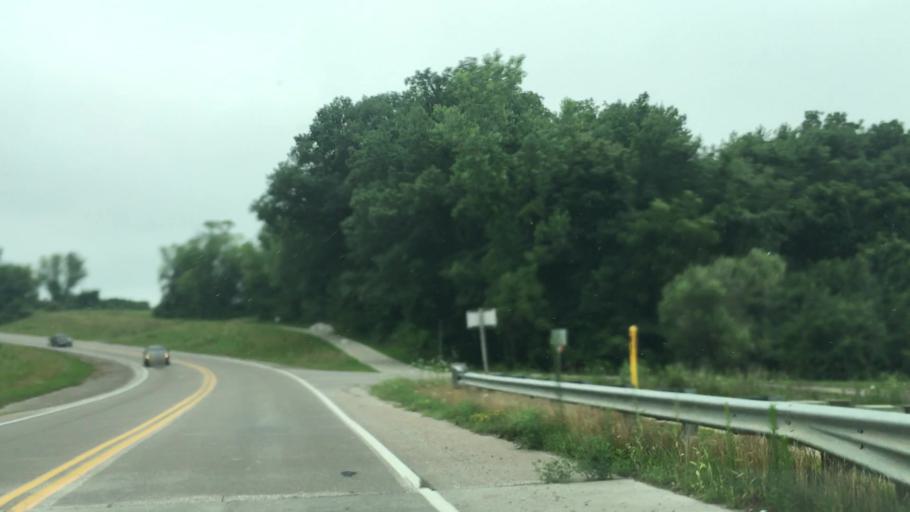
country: US
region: Iowa
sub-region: Johnson County
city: Iowa City
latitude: 41.6932
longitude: -91.5472
